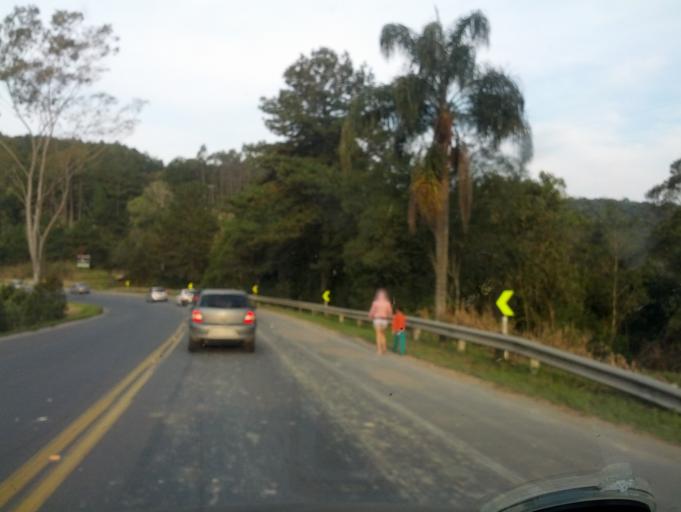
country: BR
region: Santa Catarina
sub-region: Otacilio Costa
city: Otacilio Costa
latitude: -27.2834
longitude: -50.0725
